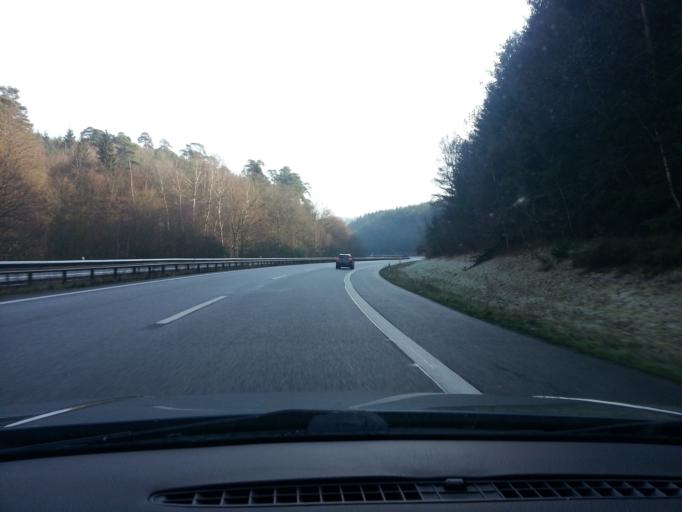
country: DE
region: Rheinland-Pfalz
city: Rodalben
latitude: 49.2155
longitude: 7.6535
